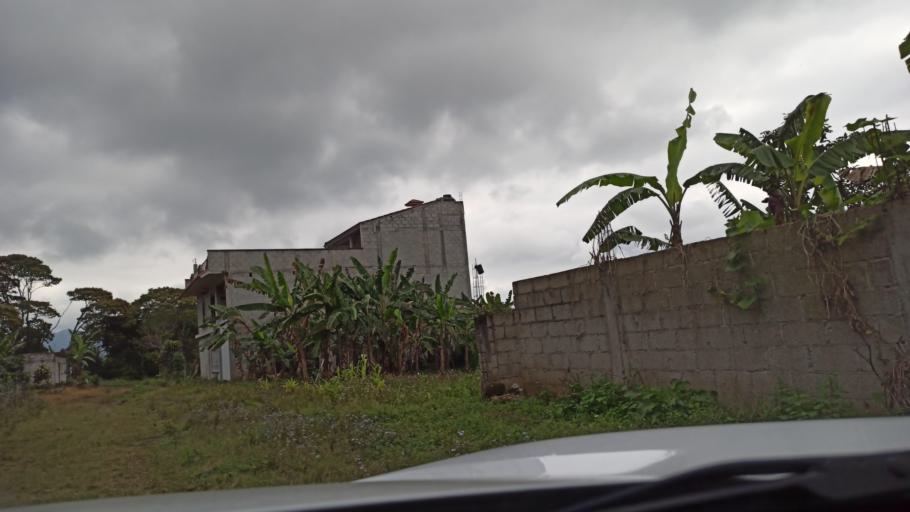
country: MX
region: Veracruz
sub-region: Fortin
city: Santa Lucia Potrerillo
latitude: 18.9664
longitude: -97.0236
